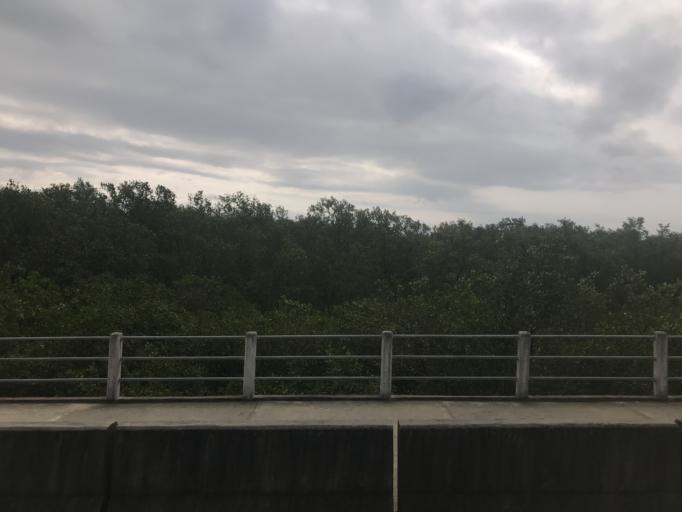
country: BR
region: Santa Catarina
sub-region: Florianopolis
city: Costeira do Pirajubae
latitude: -27.6521
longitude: -48.5234
